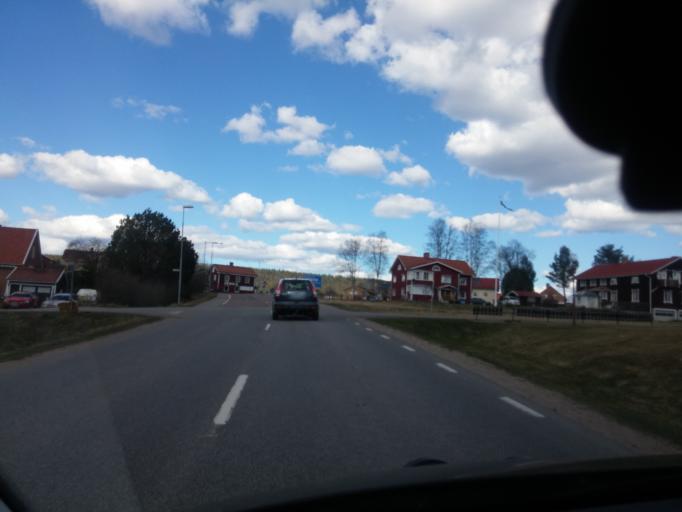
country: SE
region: Gaevleborg
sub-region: Ljusdals Kommun
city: Farila
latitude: 61.7968
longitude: 15.8372
